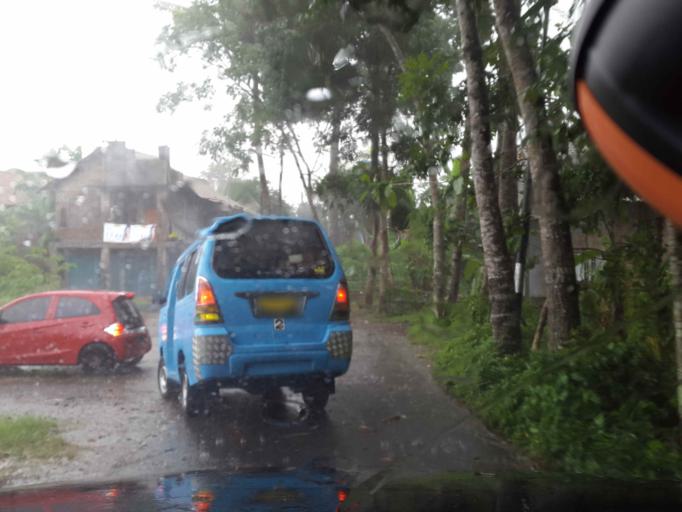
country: ID
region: Central Java
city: Salatiga
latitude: -7.3073
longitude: 110.4787
